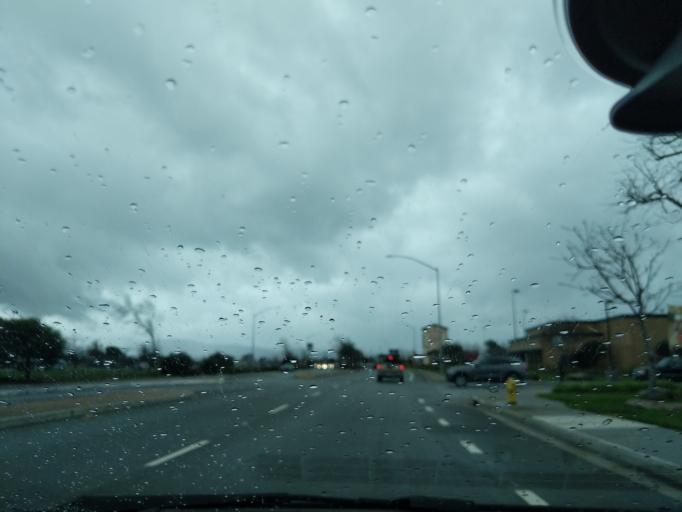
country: US
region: California
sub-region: Monterey County
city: Boronda
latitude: 36.7064
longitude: -121.6662
